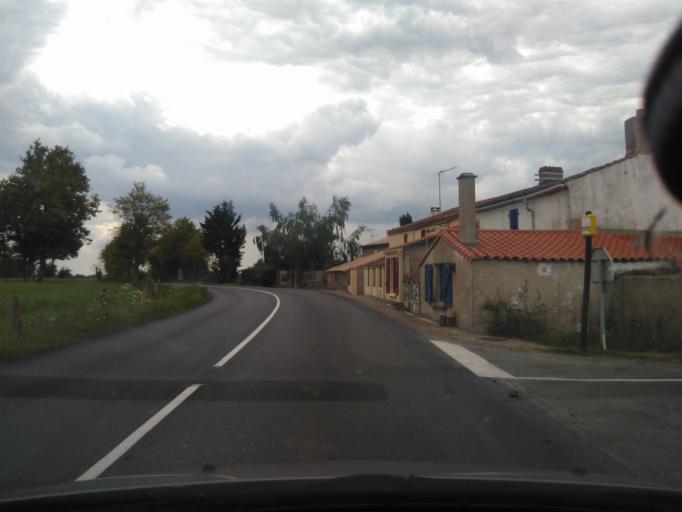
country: FR
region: Pays de la Loire
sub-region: Departement de la Vendee
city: Mouilleron-le-Captif
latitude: 46.7086
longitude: -1.4153
